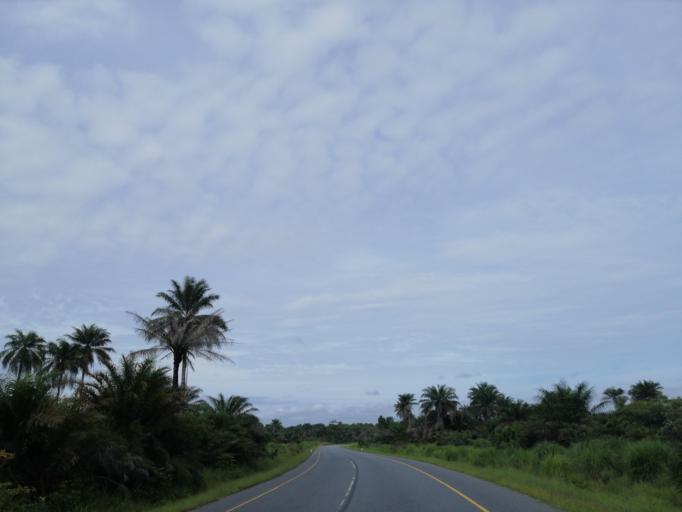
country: SL
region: Northern Province
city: Port Loko
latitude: 8.7692
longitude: -12.8837
